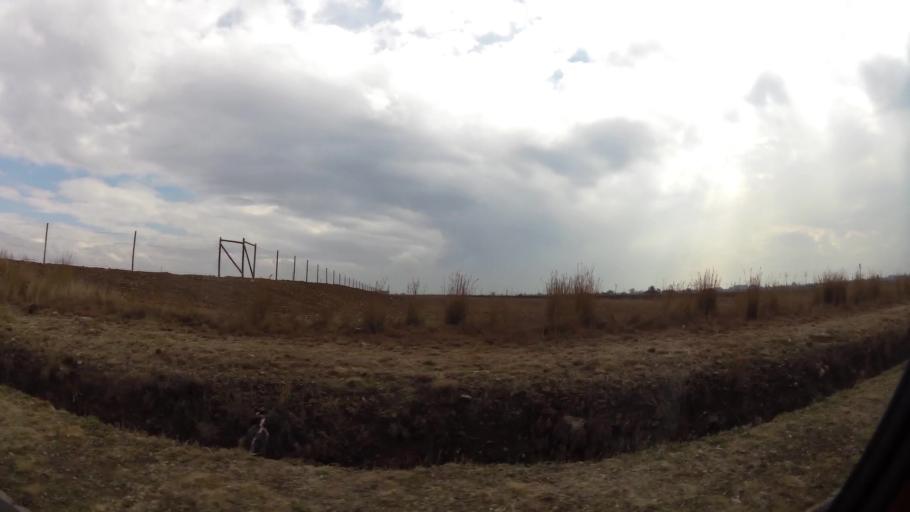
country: ZA
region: Gauteng
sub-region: Sedibeng District Municipality
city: Vanderbijlpark
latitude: -26.7207
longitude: 27.8825
